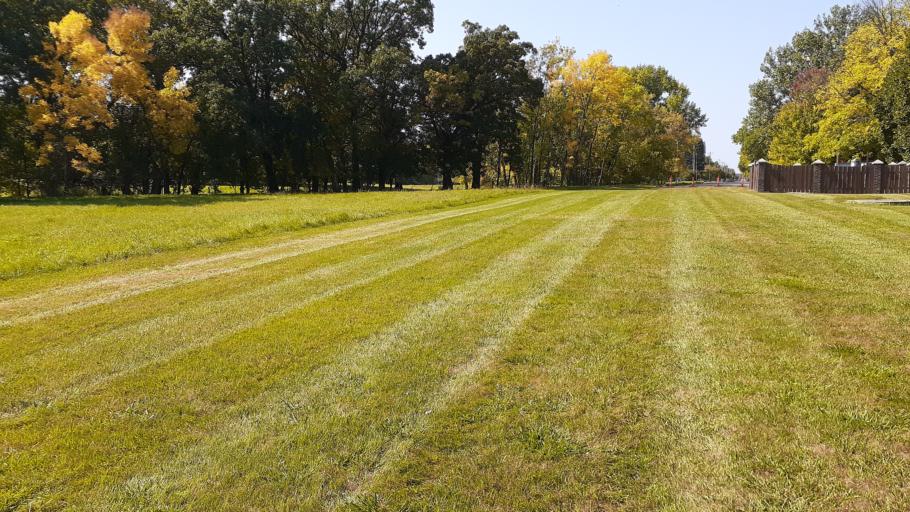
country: US
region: Minnesota
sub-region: Clay County
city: Oakport
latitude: 46.9195
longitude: -96.7628
